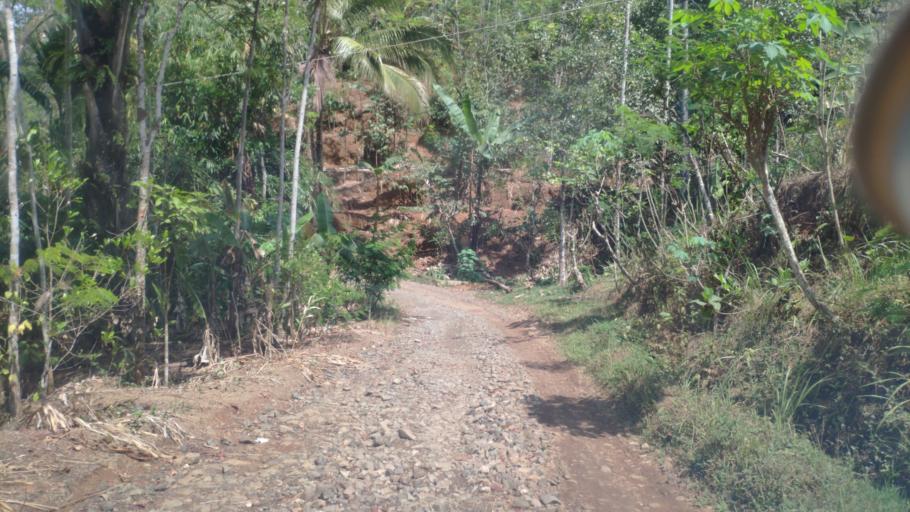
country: ID
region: Central Java
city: Purbalingga
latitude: -7.3447
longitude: 109.6134
